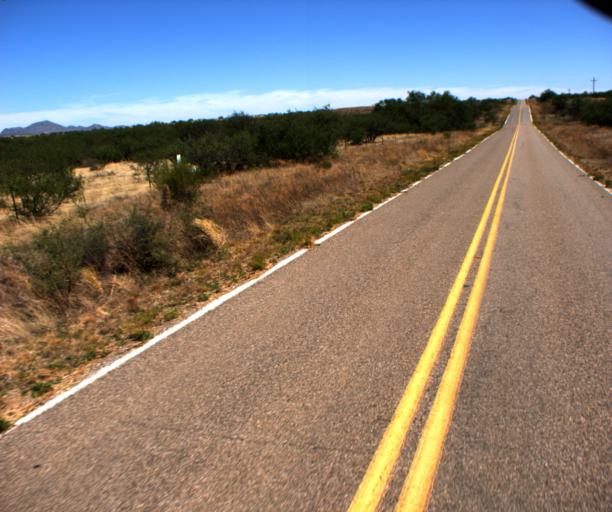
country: US
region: Arizona
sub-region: Pima County
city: Sells
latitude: 31.5613
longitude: -111.5388
